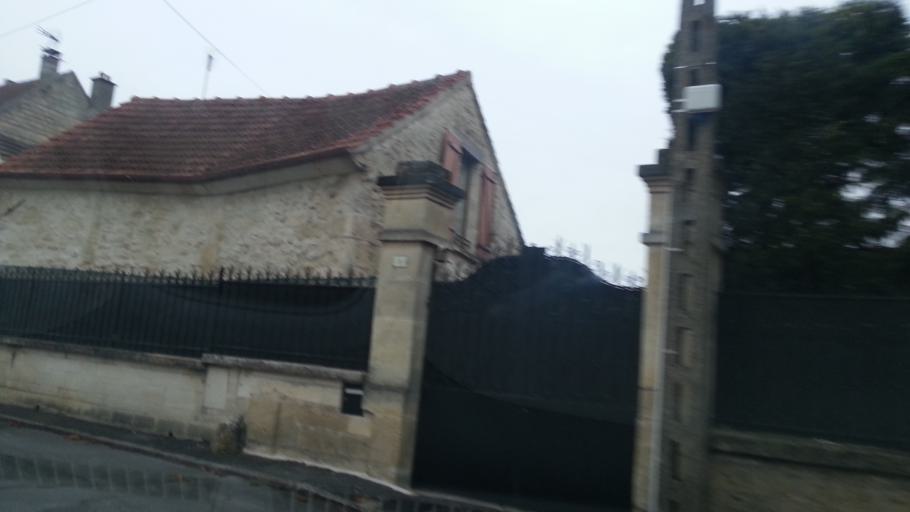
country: FR
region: Picardie
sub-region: Departement de l'Oise
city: Saint-Maximin
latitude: 49.2215
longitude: 2.4519
